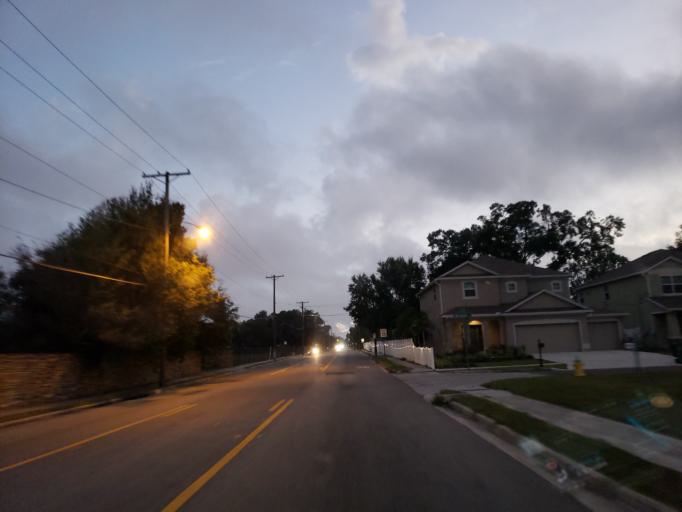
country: US
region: Florida
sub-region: Hillsborough County
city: Tampa
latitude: 27.9765
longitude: -82.4677
